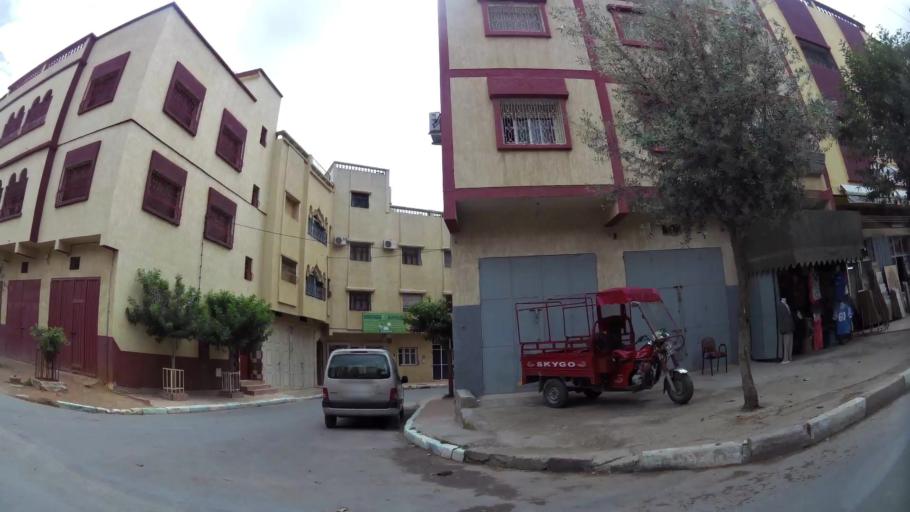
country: MA
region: Rabat-Sale-Zemmour-Zaer
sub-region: Khemisset
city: Tiflet
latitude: 33.8919
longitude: -6.3213
